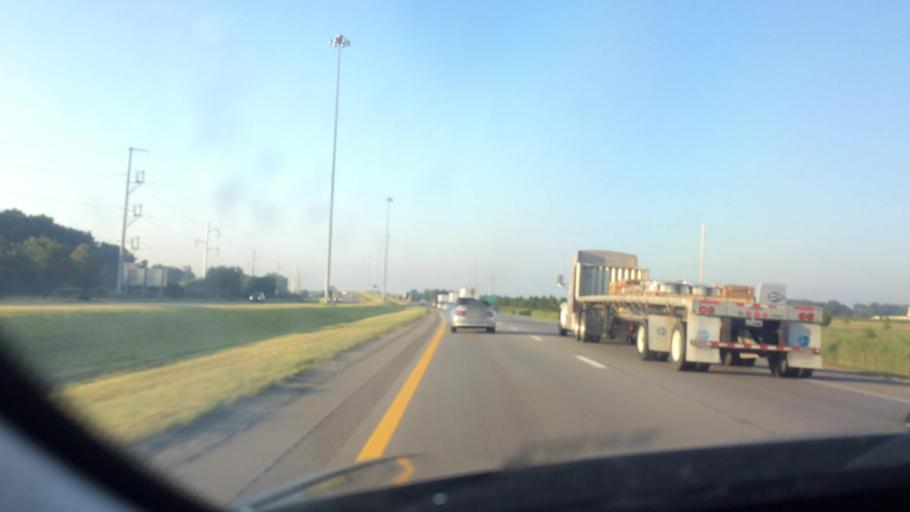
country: US
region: Ohio
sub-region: Lucas County
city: Maumee
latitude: 41.5683
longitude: -83.6911
